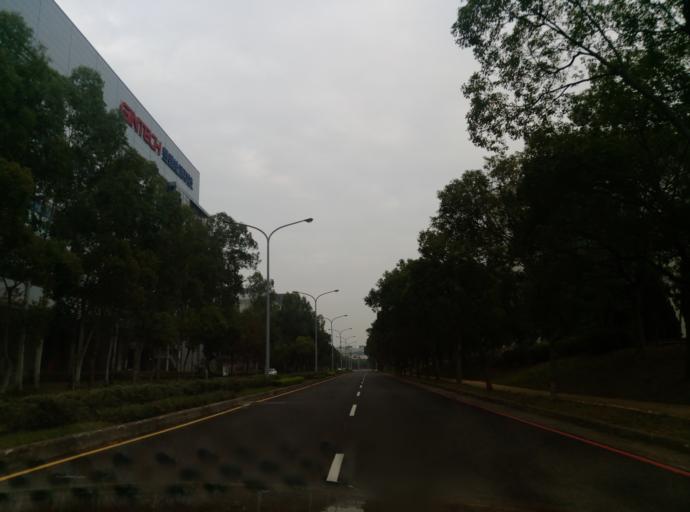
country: TW
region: Taiwan
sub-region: Hsinchu
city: Hsinchu
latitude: 24.7071
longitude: 120.9118
